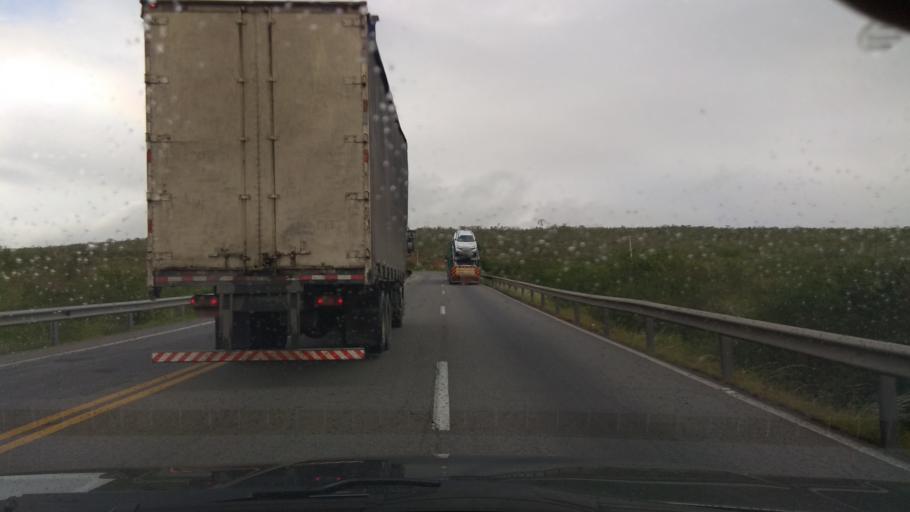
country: BR
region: Bahia
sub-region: Santa Ines
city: Santa Ines
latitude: -13.0409
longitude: -39.9675
